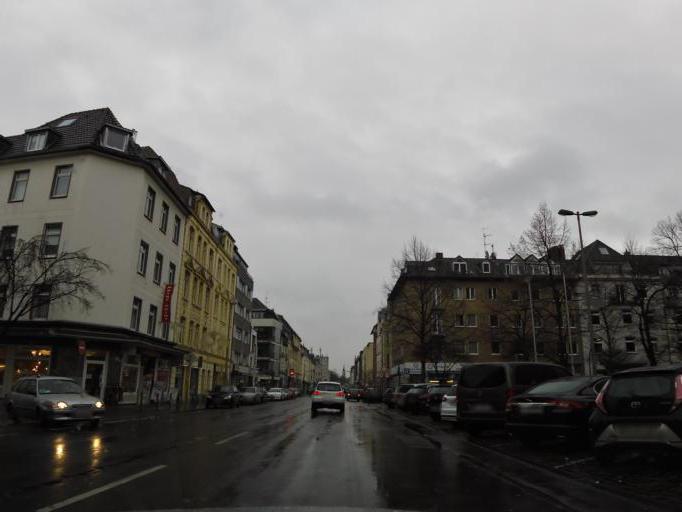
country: DE
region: North Rhine-Westphalia
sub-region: Regierungsbezirk Koln
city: Neustadt/Sued
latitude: 50.9191
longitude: 6.9263
